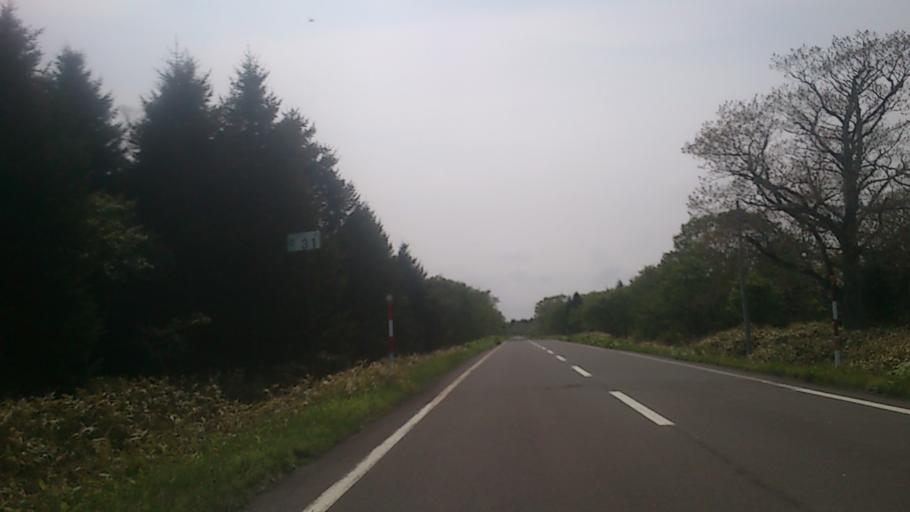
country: JP
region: Hokkaido
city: Nemuro
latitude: 43.2115
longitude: 145.3670
